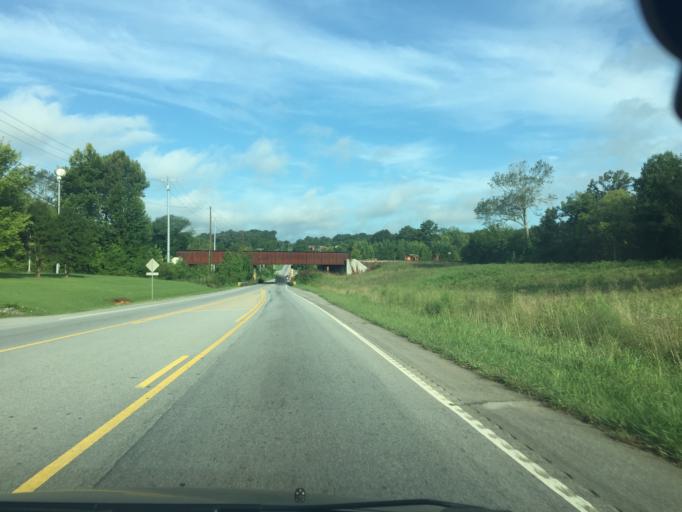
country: US
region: Tennessee
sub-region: Hamilton County
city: Harrison
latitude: 35.0721
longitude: -85.1581
